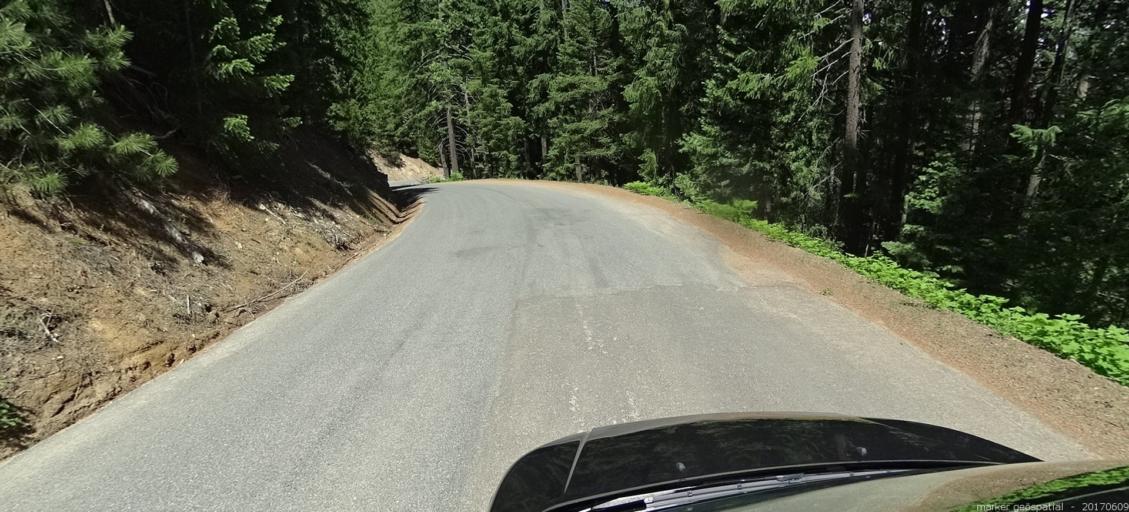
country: US
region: California
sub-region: Siskiyou County
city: Yreka
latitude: 41.4290
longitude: -122.9483
